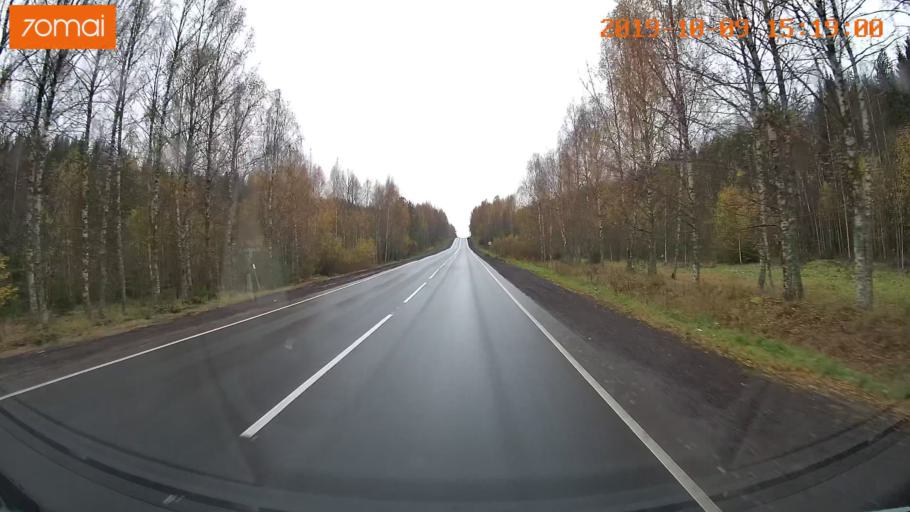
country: RU
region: Kostroma
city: Susanino
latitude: 58.0803
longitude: 41.5640
